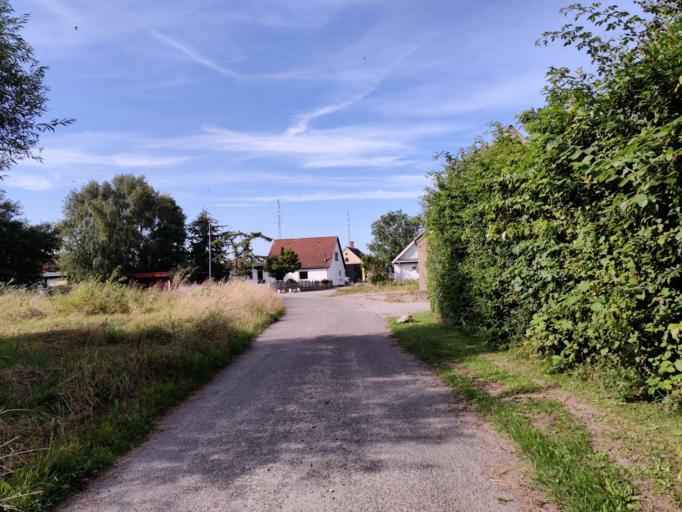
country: DK
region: Zealand
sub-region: Guldborgsund Kommune
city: Nykobing Falster
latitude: 54.6439
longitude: 11.8977
